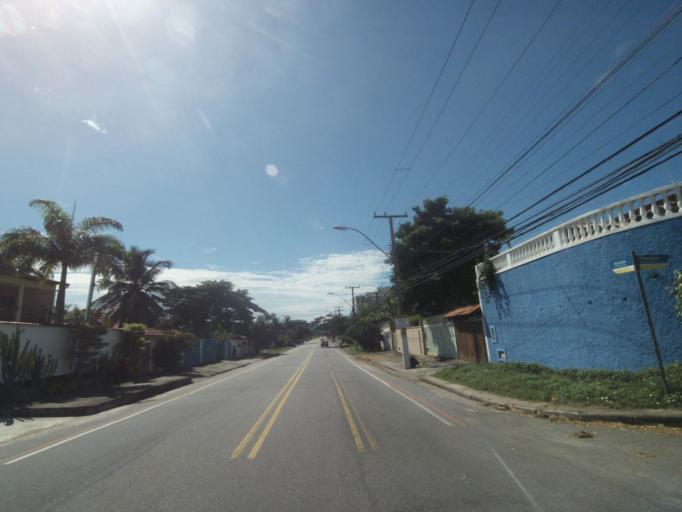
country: BR
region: Rio de Janeiro
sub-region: Niteroi
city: Niteroi
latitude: -22.9526
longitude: -43.0824
